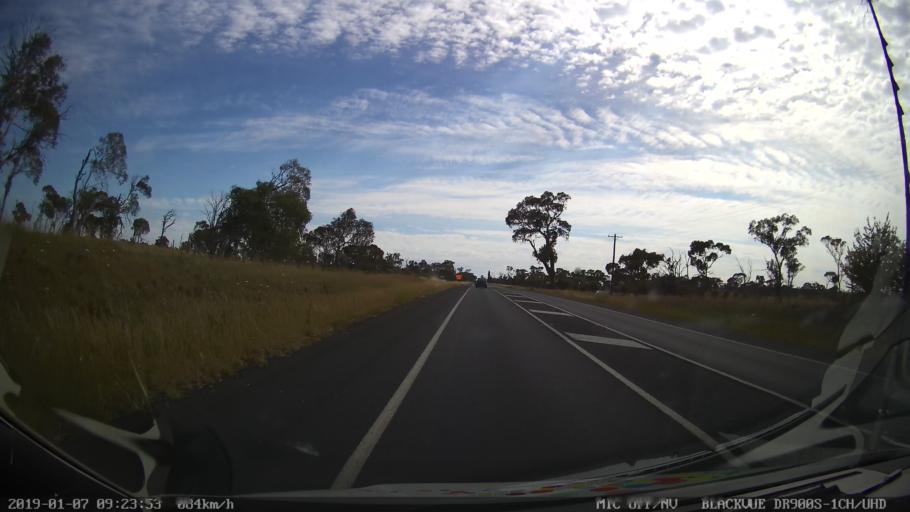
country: AU
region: New South Wales
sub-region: Armidale Dumaresq
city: Armidale
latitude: -30.5523
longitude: 151.5897
